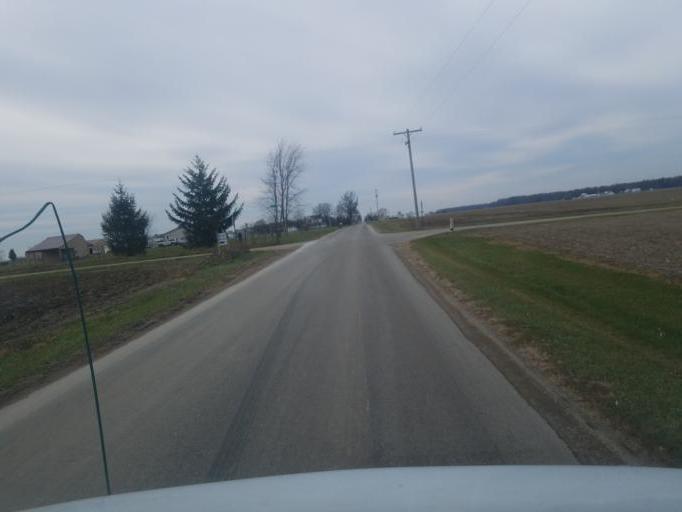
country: US
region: Indiana
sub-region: Adams County
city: Geneva
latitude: 40.6151
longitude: -84.8682
